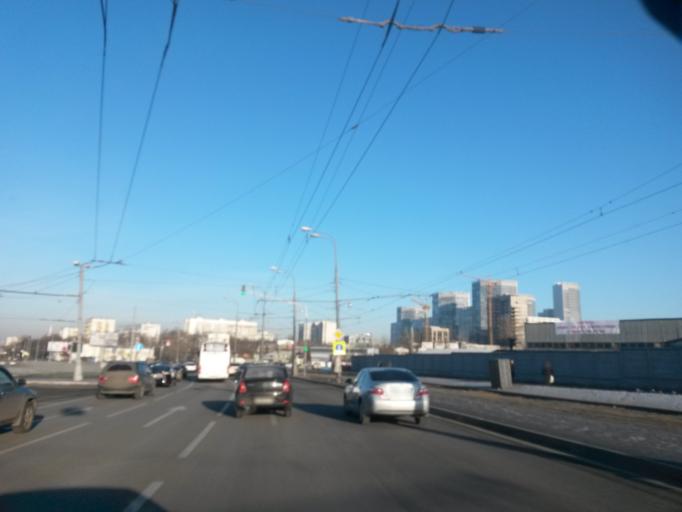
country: RU
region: Moscow
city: Nagornyy
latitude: 55.6722
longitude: 37.6272
